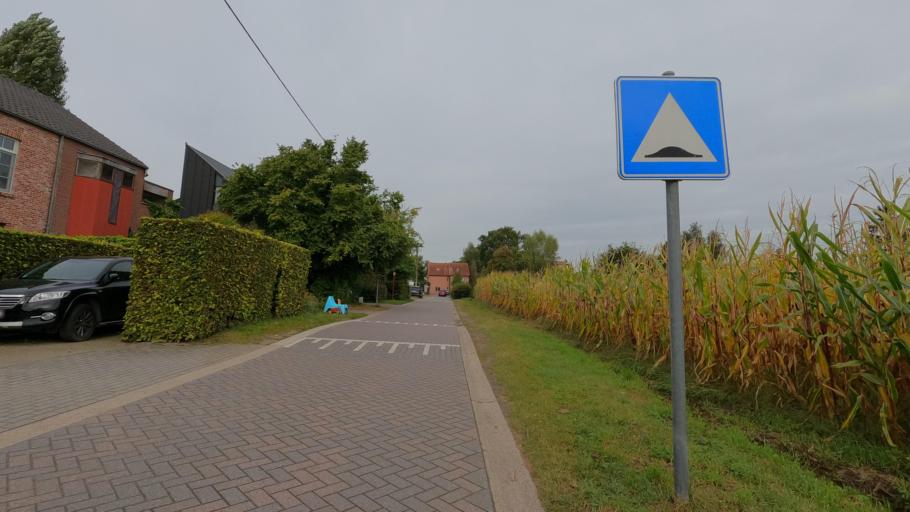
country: BE
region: Flanders
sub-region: Provincie Antwerpen
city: Schilde
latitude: 51.2951
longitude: 4.5662
